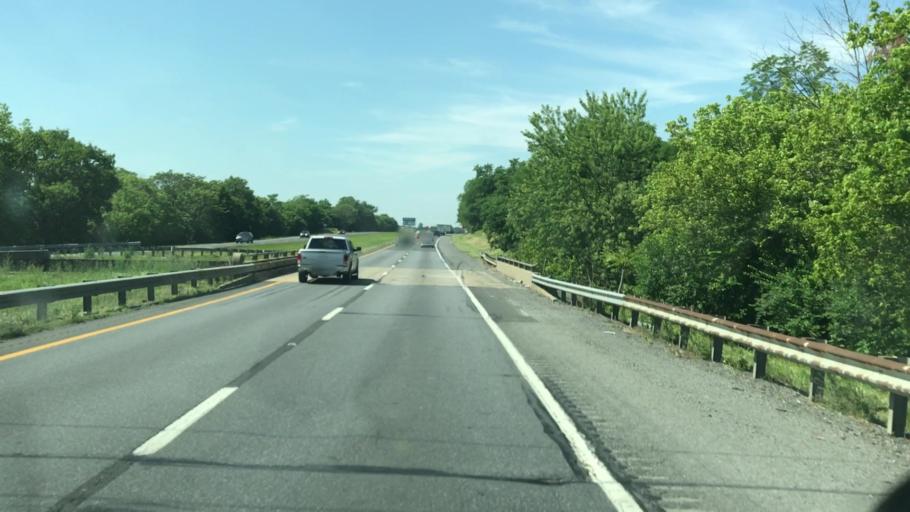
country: US
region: West Virginia
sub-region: Berkeley County
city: Inwood
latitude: 39.3405
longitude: -78.0619
